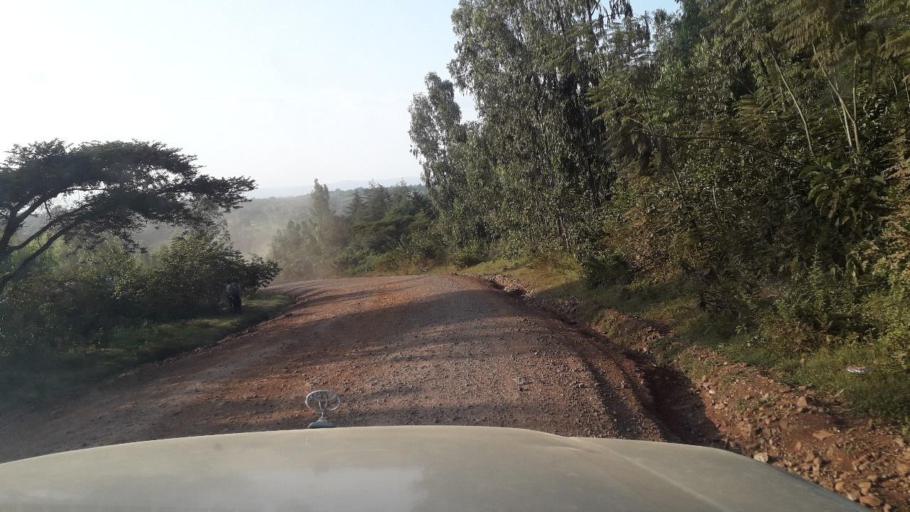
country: ET
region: Oromiya
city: Jima
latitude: 7.5731
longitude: 36.8597
